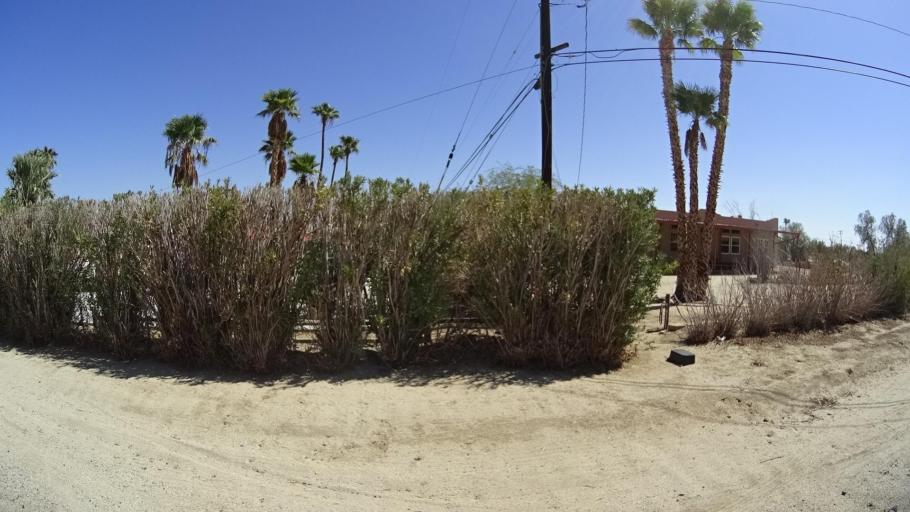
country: US
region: California
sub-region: San Diego County
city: Borrego Springs
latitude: 33.2348
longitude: -116.3801
